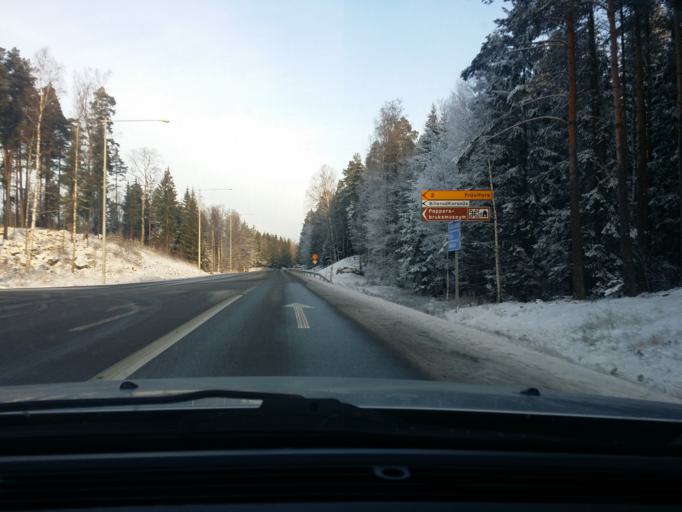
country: SE
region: OErebro
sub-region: Lindesbergs Kommun
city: Frovi
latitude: 59.4910
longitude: 15.3761
